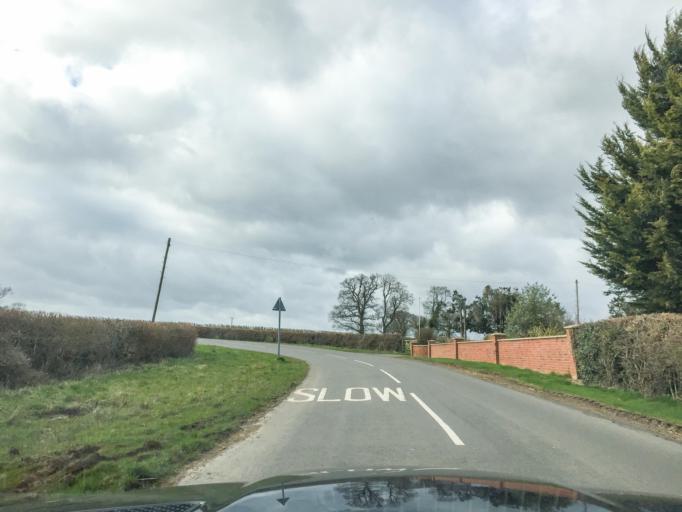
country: GB
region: England
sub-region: Warwickshire
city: Shipston on Stour
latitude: 52.0621
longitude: -1.5468
